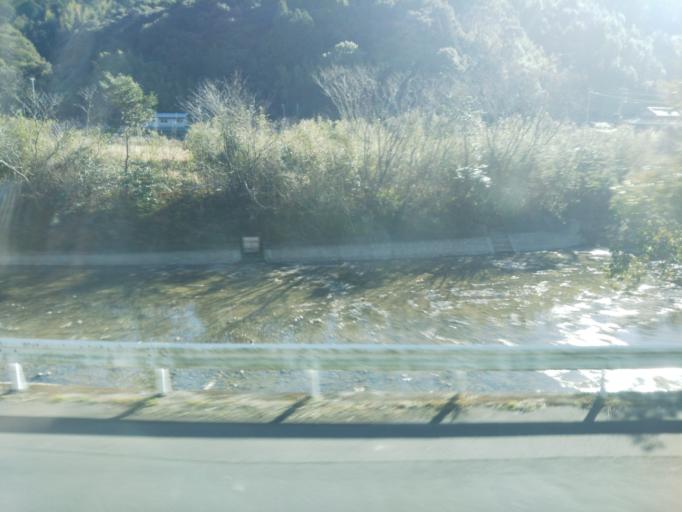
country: JP
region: Kochi
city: Nakamura
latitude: 33.1106
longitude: 133.1042
